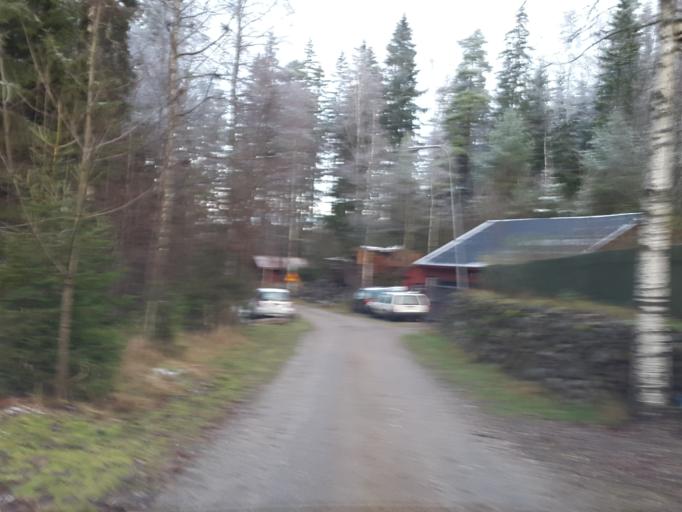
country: SE
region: Vaestra Goetaland
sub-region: Vargarda Kommun
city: Jonstorp
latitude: 57.8468
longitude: 12.6814
